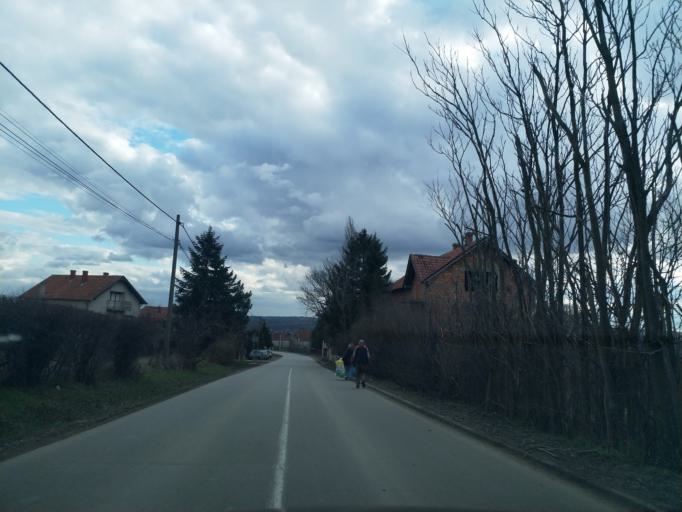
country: RS
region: Central Serbia
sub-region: Belgrade
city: Grocka
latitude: 44.5958
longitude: 20.7258
